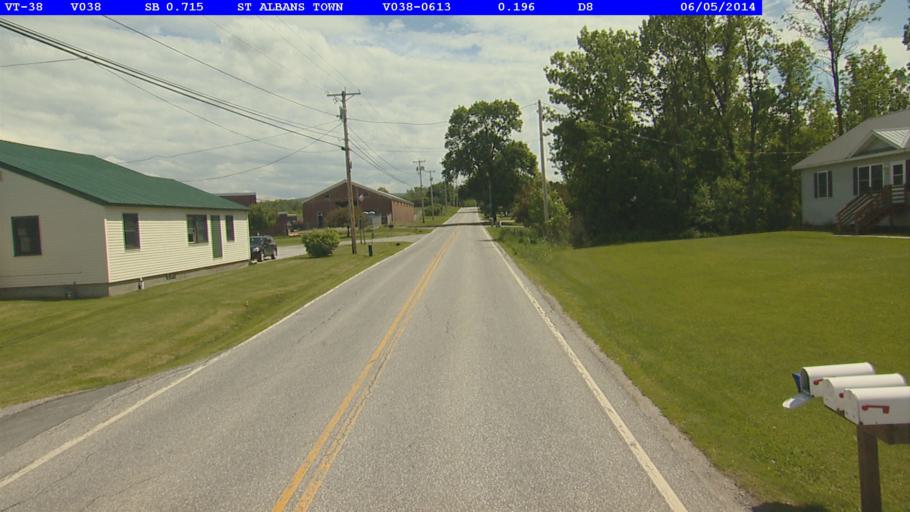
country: US
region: Vermont
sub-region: Franklin County
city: Saint Albans
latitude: 44.8266
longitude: -73.0907
